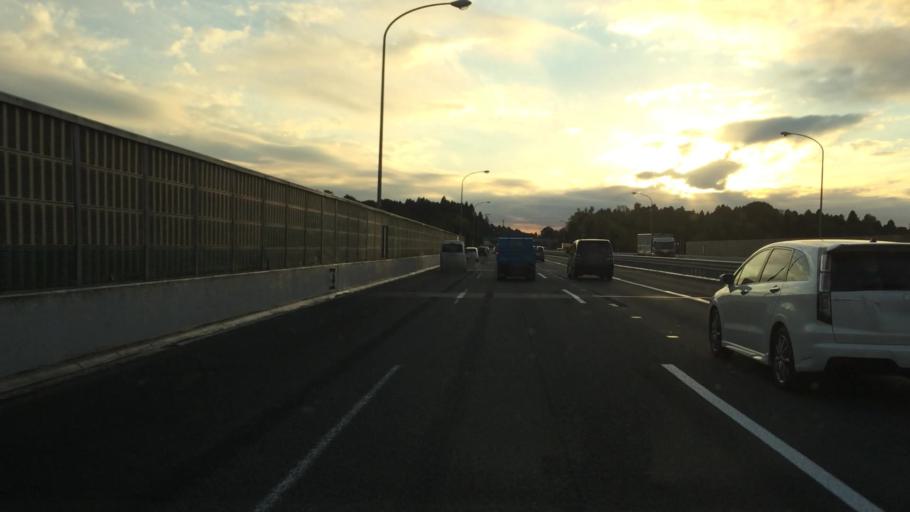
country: JP
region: Chiba
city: Shisui
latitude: 35.6948
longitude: 140.2539
